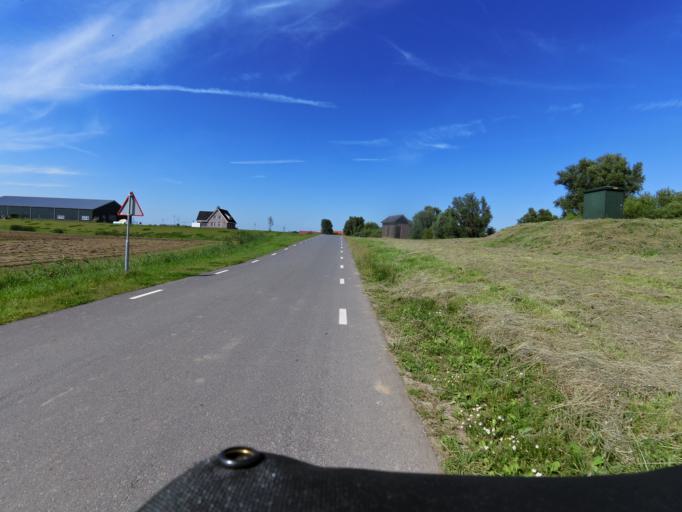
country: NL
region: North Brabant
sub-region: Gemeente Werkendam
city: Werkendam
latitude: 51.7666
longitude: 4.8584
